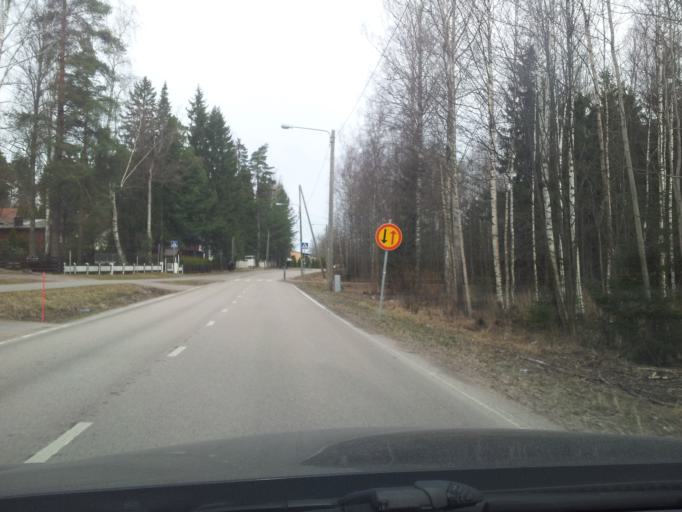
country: FI
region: Uusimaa
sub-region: Helsinki
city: Kilo
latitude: 60.1939
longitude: 24.7952
